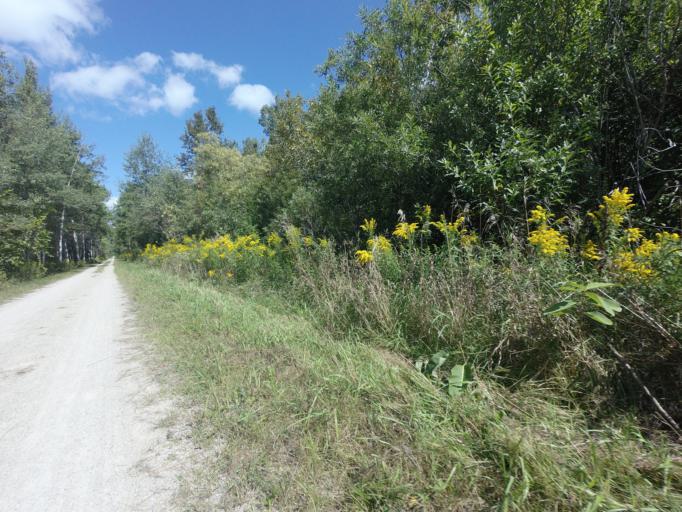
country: CA
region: Ontario
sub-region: Wellington County
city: Guelph
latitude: 43.7553
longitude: -80.3215
